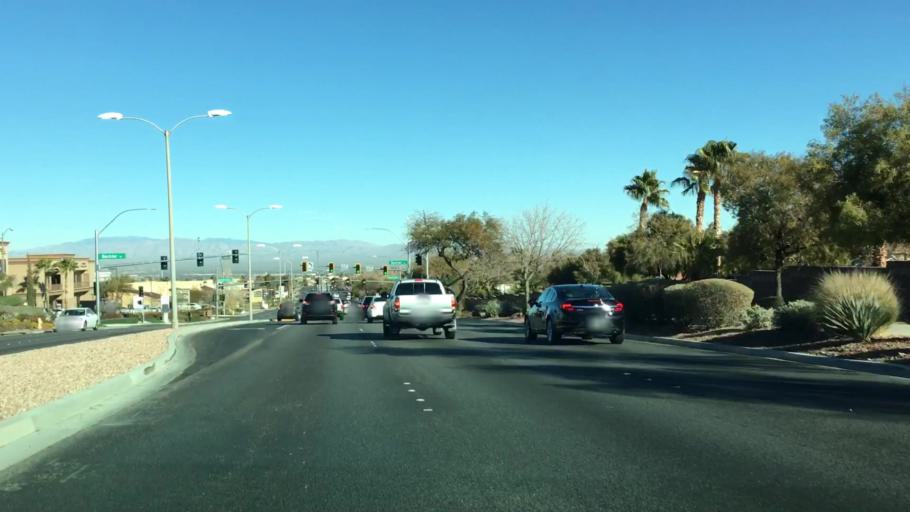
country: US
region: Nevada
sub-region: Clark County
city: Whitney
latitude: 35.9871
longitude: -115.1009
